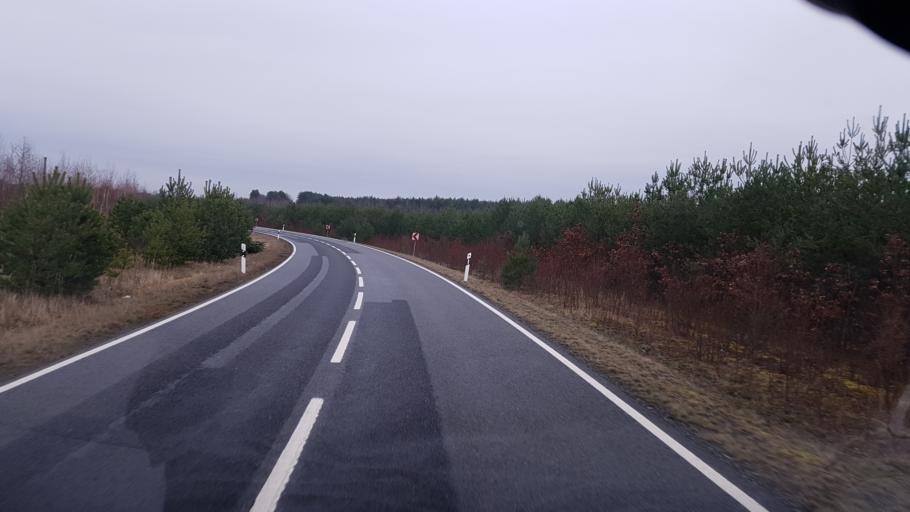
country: DE
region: Brandenburg
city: Schipkau
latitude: 51.5045
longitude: 13.8617
